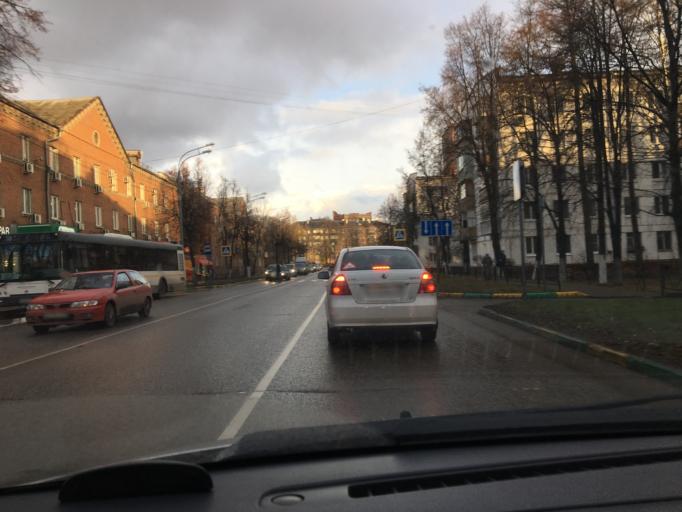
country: RU
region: Moskovskaya
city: Vidnoye
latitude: 55.5538
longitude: 37.6954
